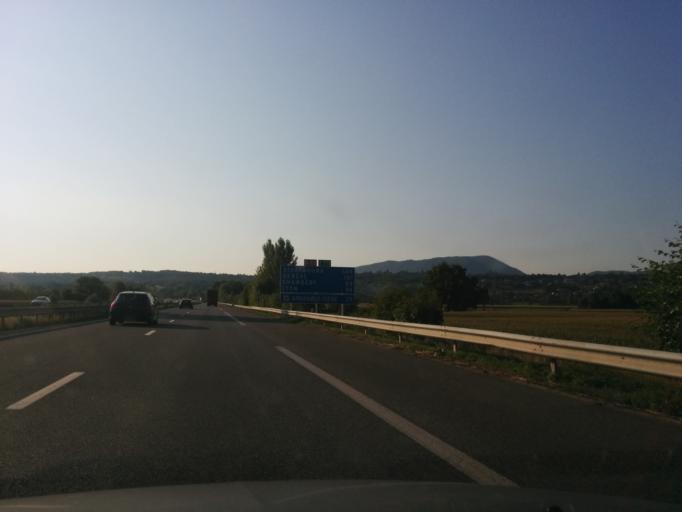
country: FR
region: Rhone-Alpes
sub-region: Departement de l'Isere
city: Saint-Jean-de-Moirans
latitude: 45.3298
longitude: 5.5924
